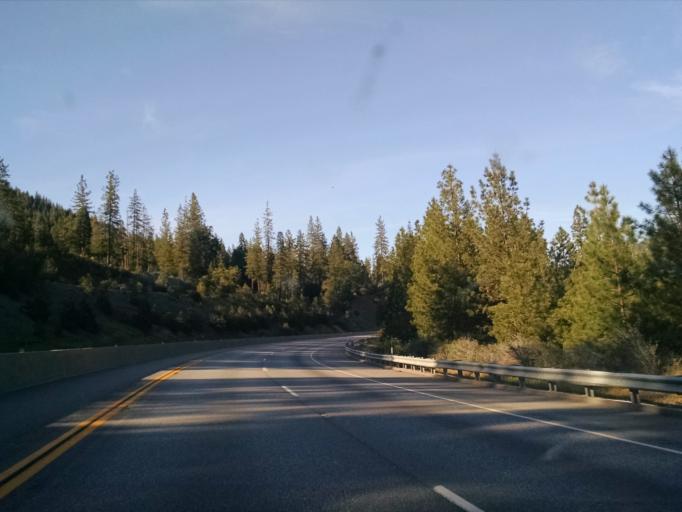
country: US
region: California
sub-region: Siskiyou County
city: Dunsmuir
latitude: 41.0536
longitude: -122.3793
